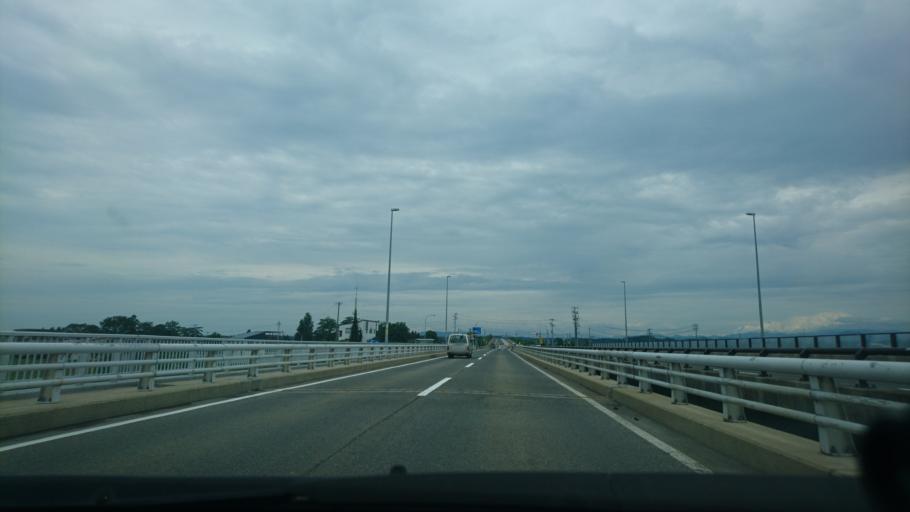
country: JP
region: Akita
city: Omagari
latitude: 39.4860
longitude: 140.4539
